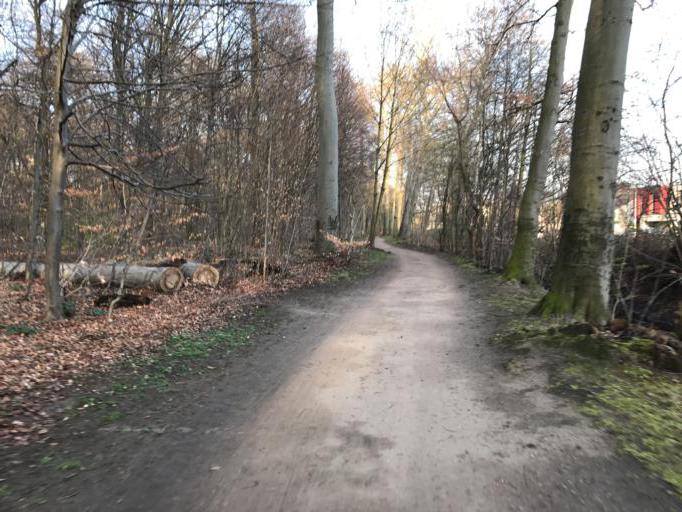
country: DE
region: Lower Saxony
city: Laatzen
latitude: 52.3516
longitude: 9.7762
